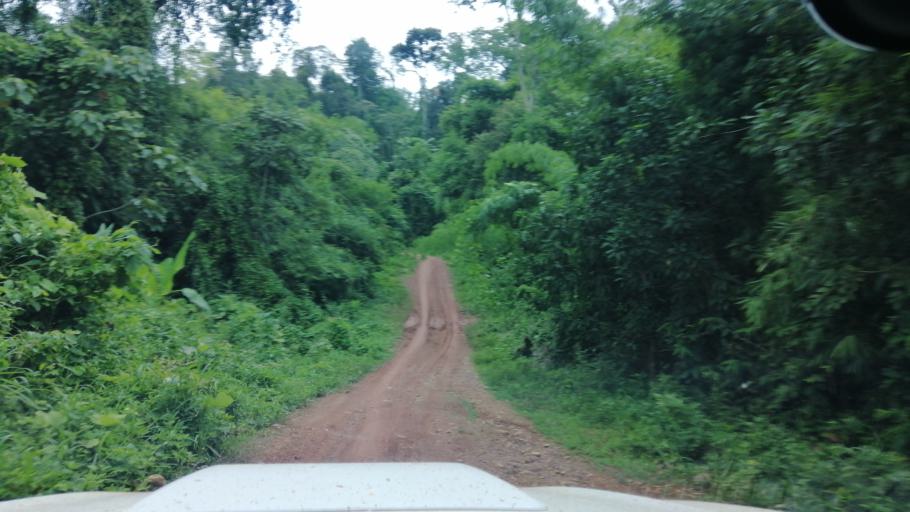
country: TH
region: Nan
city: Mae Charim
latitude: 18.7689
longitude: 101.3111
